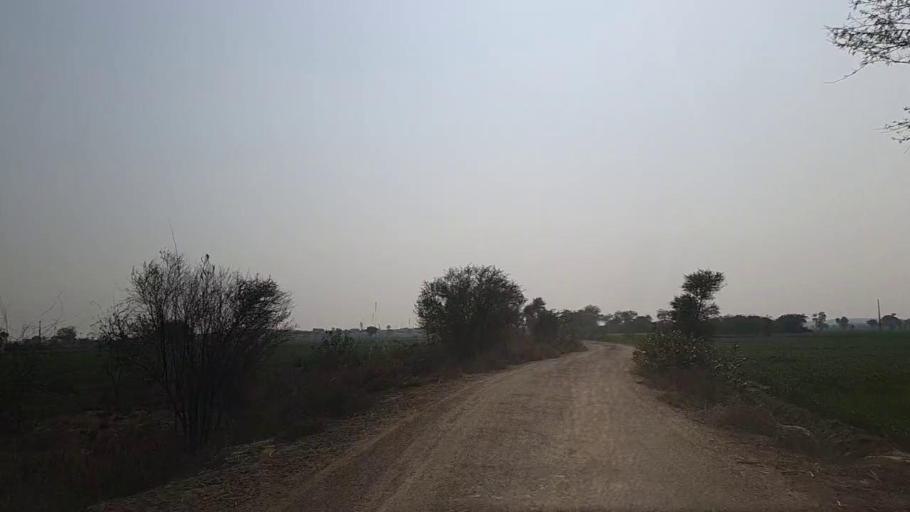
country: PK
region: Sindh
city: Jam Sahib
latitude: 26.4421
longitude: 68.5234
